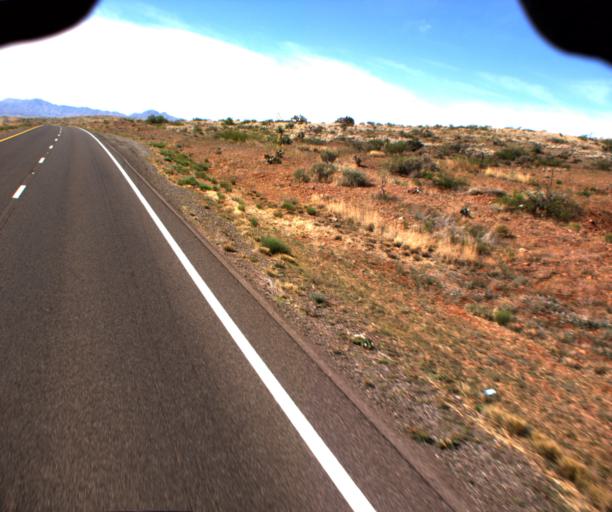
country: US
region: Arizona
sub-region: Cochise County
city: Willcox
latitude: 32.4429
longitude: -109.6639
